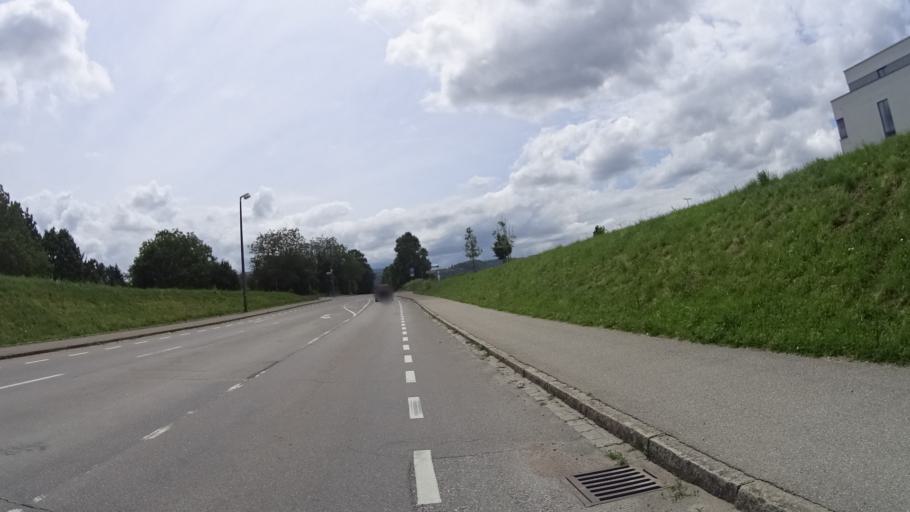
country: DE
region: Baden-Wuerttemberg
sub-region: Freiburg Region
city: Grenzach-Wyhlen
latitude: 47.5486
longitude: 7.6714
